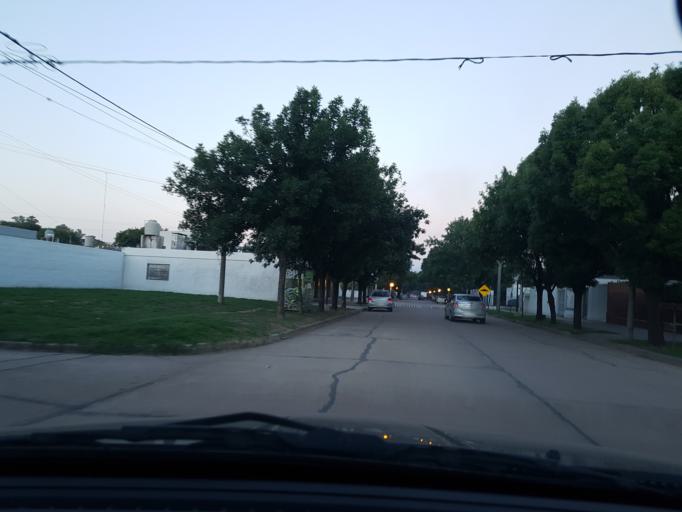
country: AR
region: Cordoba
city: General Cabrera
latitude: -32.7580
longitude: -63.7945
